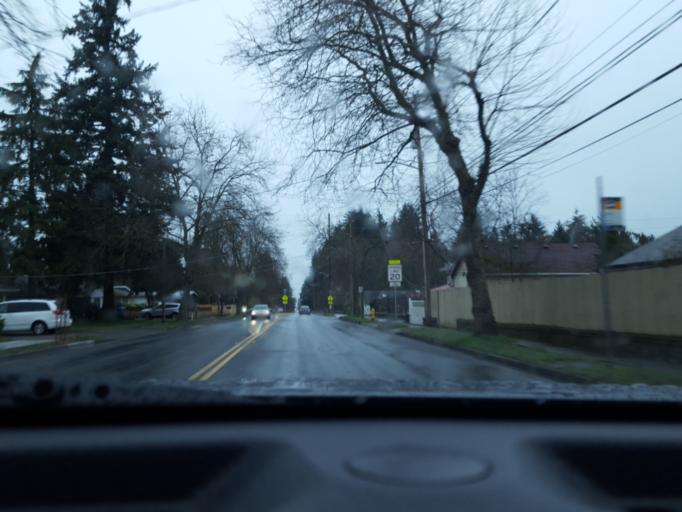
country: US
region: Washington
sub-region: King County
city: Shoreline
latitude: 47.7693
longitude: -122.3351
